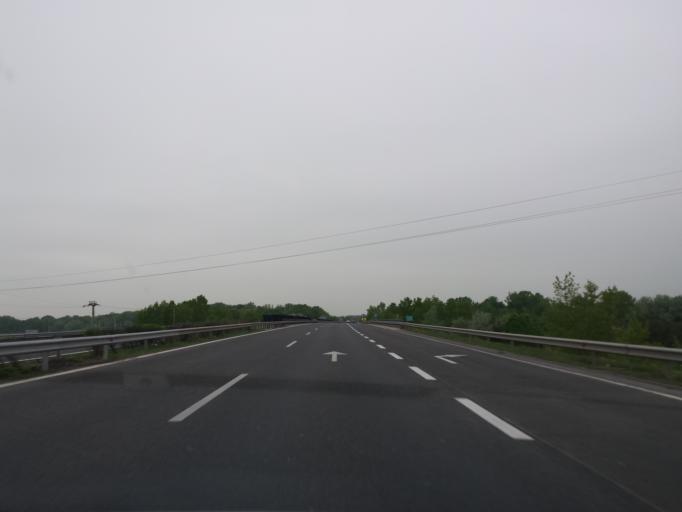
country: HU
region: Gyor-Moson-Sopron
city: Abda
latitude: 47.6773
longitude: 17.5519
